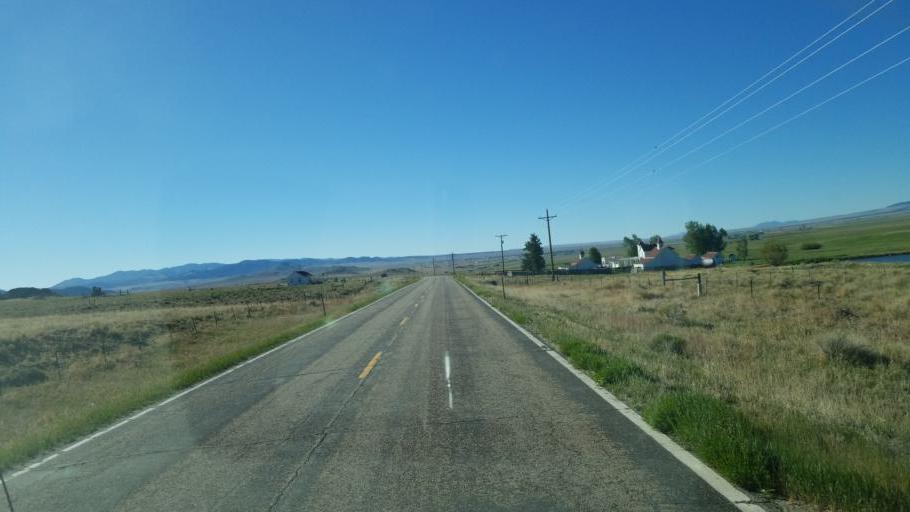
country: US
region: Colorado
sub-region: Custer County
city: Westcliffe
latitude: 38.1941
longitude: -105.5252
